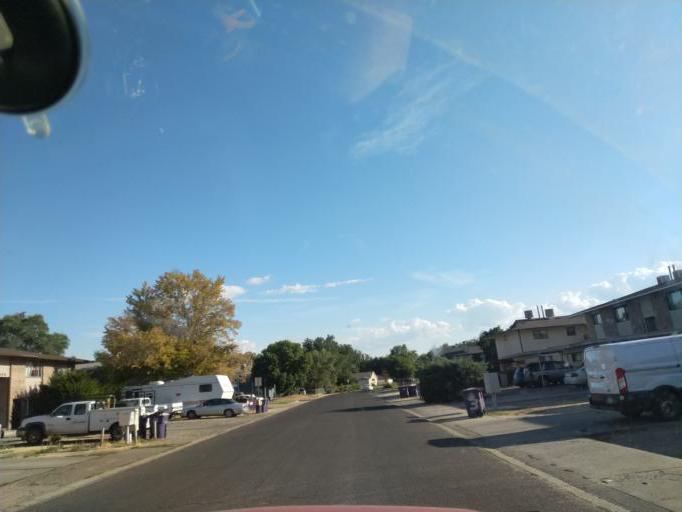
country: US
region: Colorado
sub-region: Mesa County
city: Clifton
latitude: 39.0746
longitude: -108.4566
